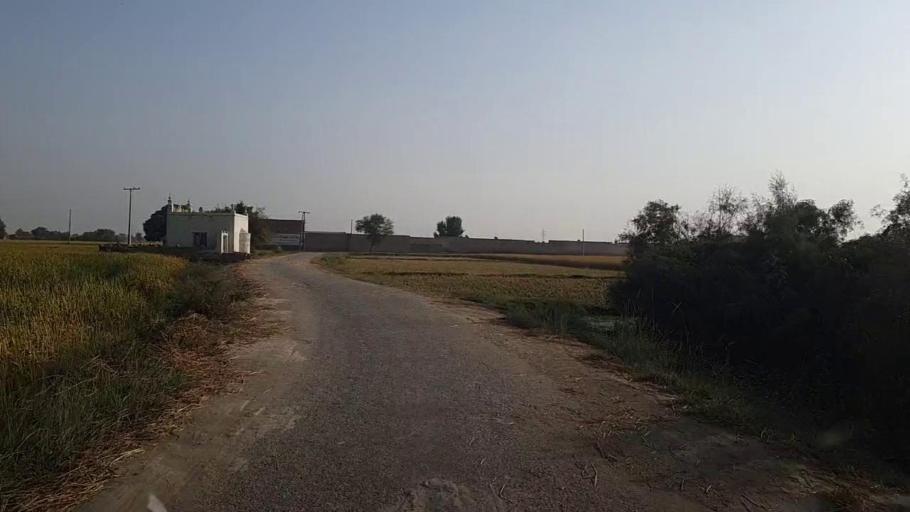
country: PK
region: Sindh
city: Kandhkot
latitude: 28.2525
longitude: 69.1600
